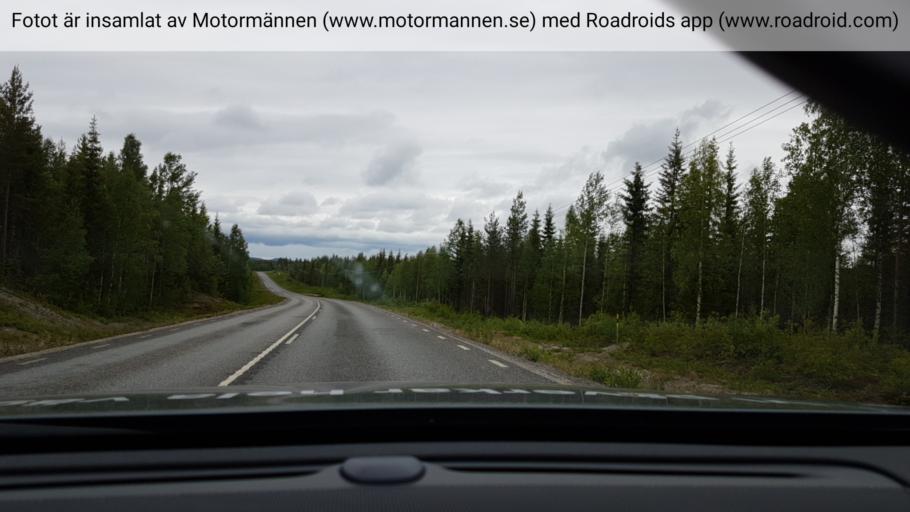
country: SE
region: Vaesterbotten
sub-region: Lycksele Kommun
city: Lycksele
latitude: 64.5424
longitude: 18.5028
